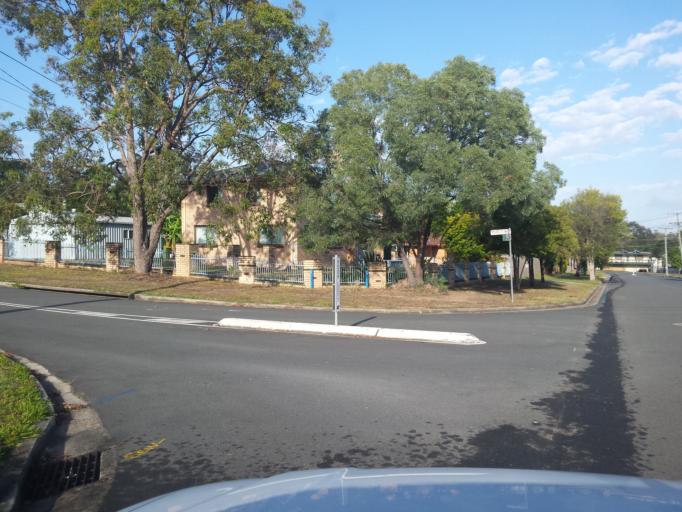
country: AU
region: Queensland
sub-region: Logan
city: Logan City
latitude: -27.6544
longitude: 153.0998
